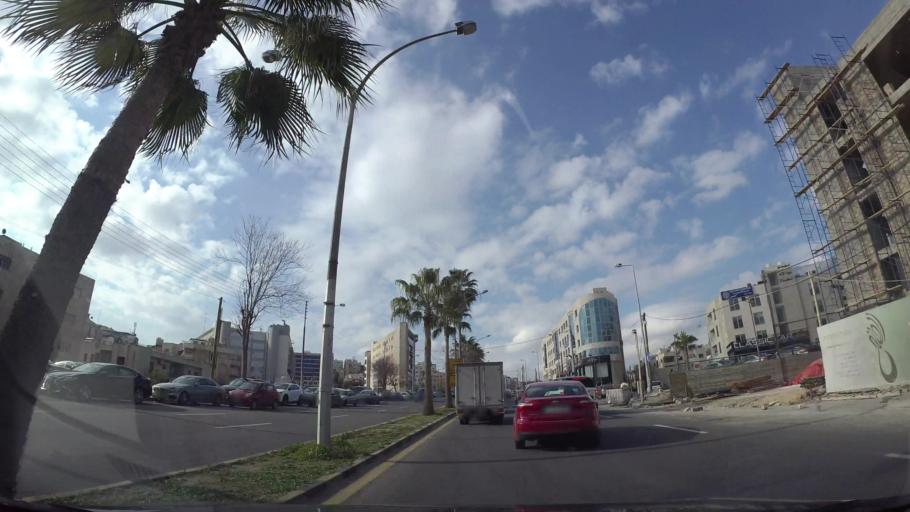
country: JO
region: Amman
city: Amman
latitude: 31.9644
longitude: 35.8882
